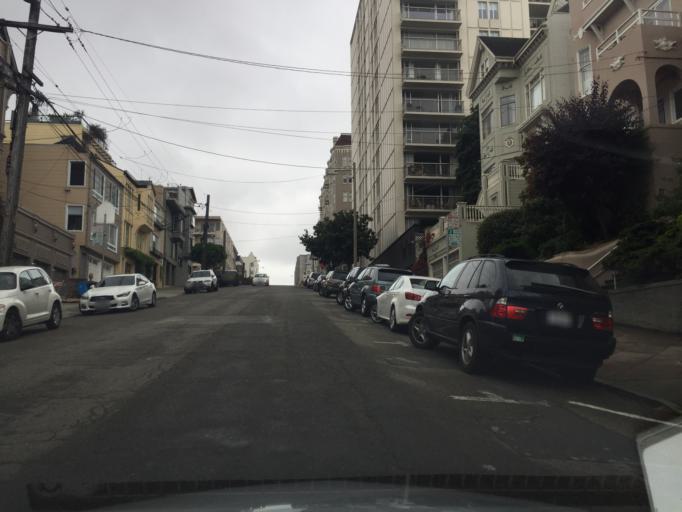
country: US
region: California
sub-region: San Francisco County
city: San Francisco
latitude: 37.7945
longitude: -122.4316
